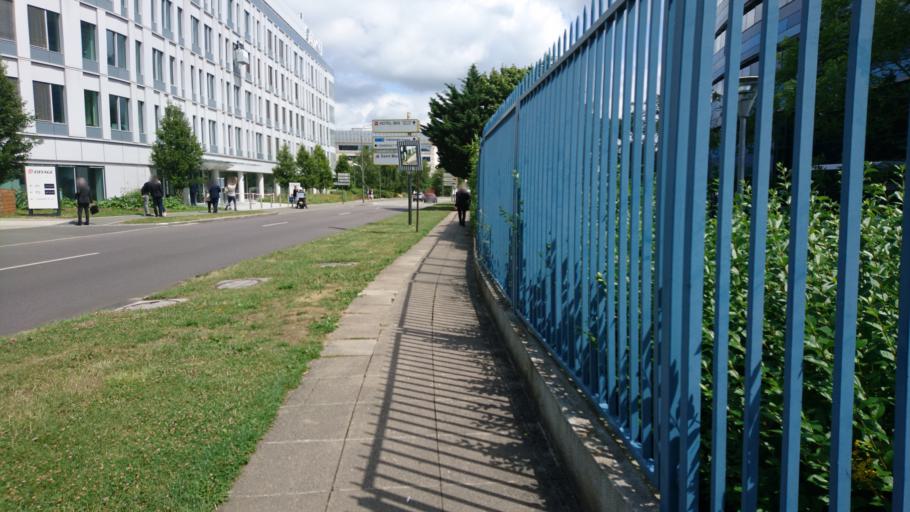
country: FR
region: Ile-de-France
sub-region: Departement des Yvelines
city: Velizy-Villacoublay
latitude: 48.7798
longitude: 2.2076
